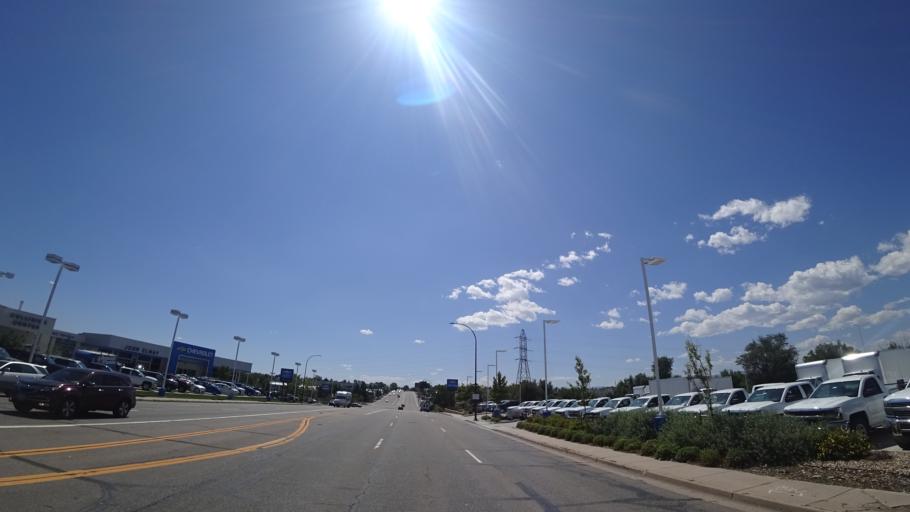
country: US
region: Colorado
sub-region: Arapahoe County
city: Englewood
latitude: 39.6219
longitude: -104.9881
